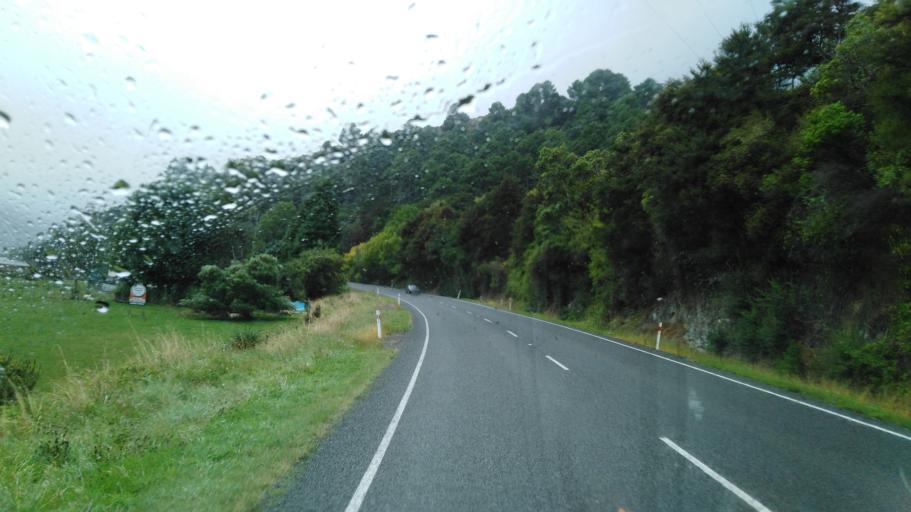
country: NZ
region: Marlborough
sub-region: Marlborough District
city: Picton
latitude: -41.2758
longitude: 173.7405
